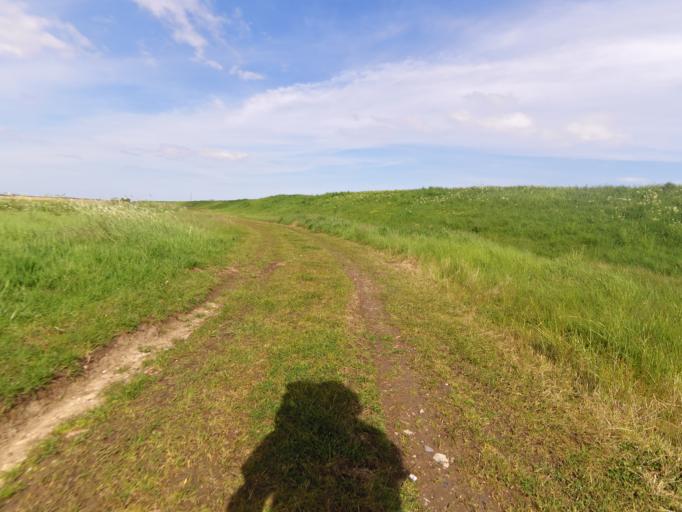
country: GB
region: England
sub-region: Norfolk
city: Great Yarmouth
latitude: 52.6075
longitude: 1.6775
